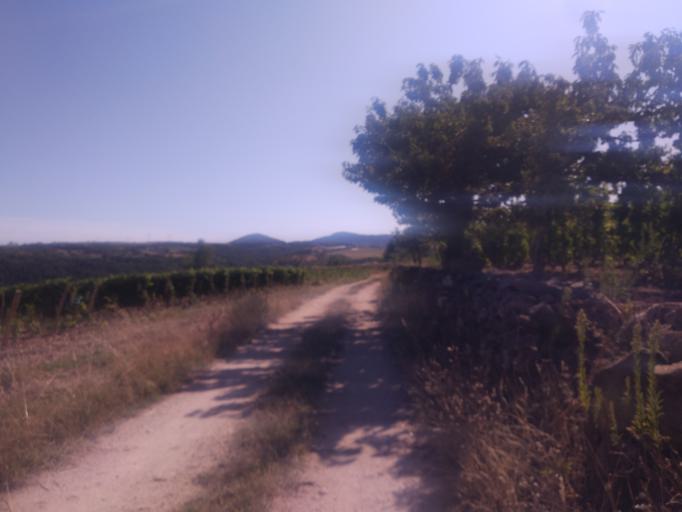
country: FR
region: Rhone-Alpes
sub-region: Departement de l'Ardeche
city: Sarras
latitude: 45.1969
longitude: 4.7692
